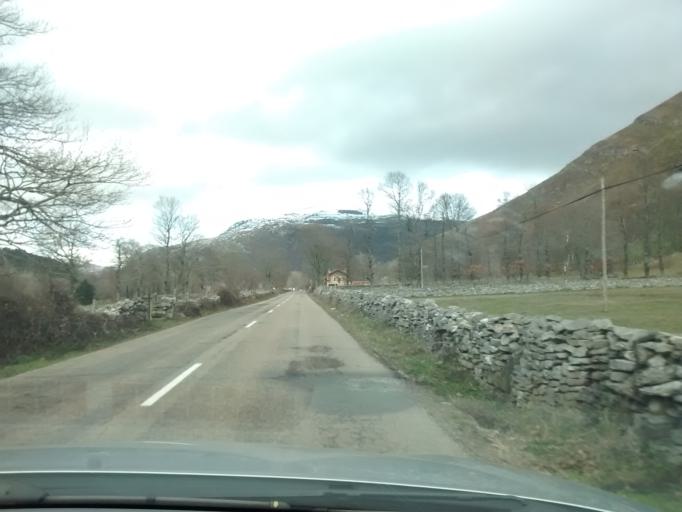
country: ES
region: Castille and Leon
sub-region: Provincia de Burgos
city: Espinosa de los Monteros
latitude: 43.1049
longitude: -3.5727
